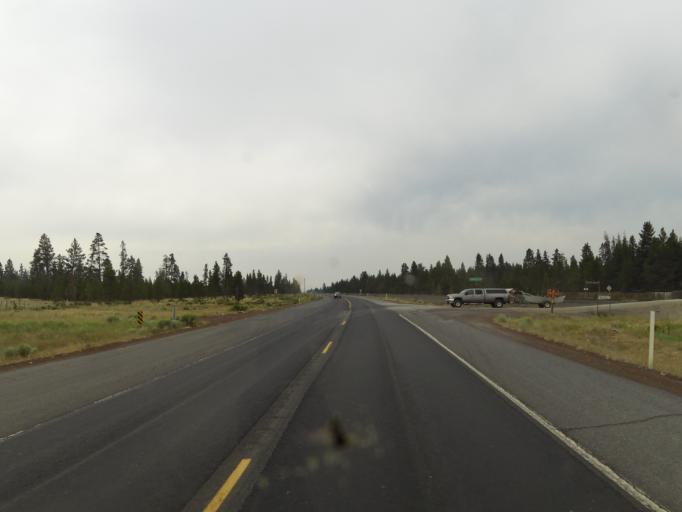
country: US
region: Oregon
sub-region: Deschutes County
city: La Pine
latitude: 43.7401
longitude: -121.4667
